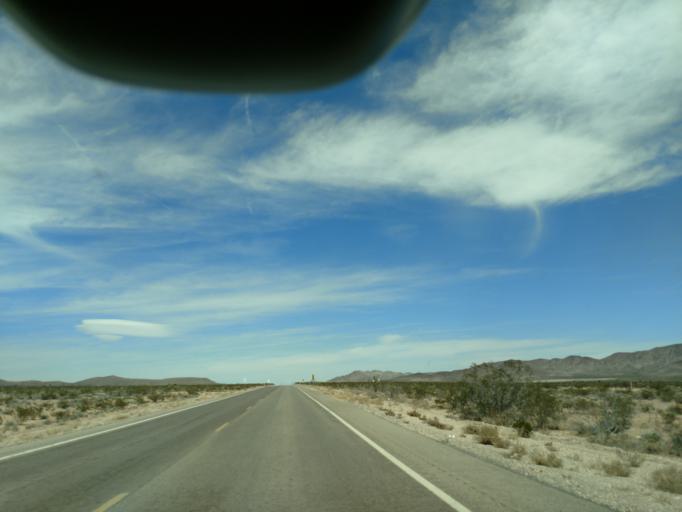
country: US
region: Nevada
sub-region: Clark County
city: Enterprise
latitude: 35.8322
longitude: -115.2802
